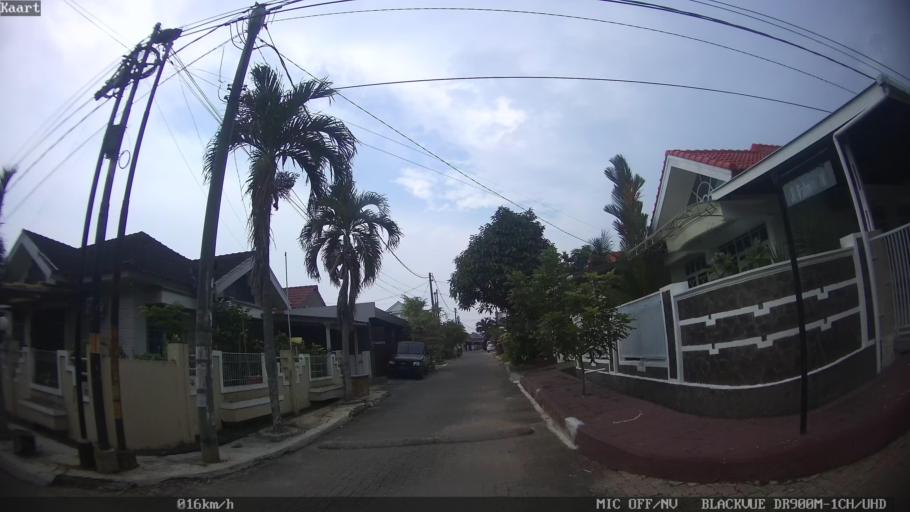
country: ID
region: Lampung
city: Bandarlampung
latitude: -5.4135
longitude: 105.2904
